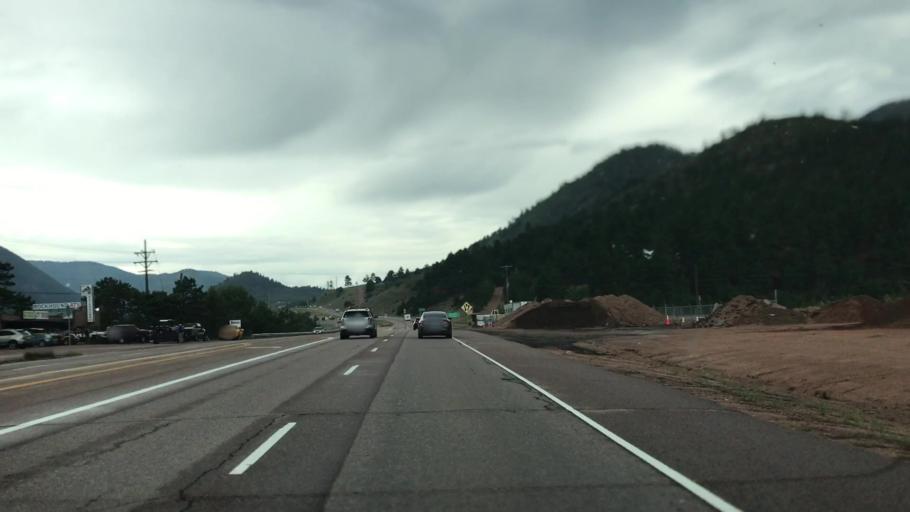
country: US
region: Colorado
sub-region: El Paso County
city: Cascade-Chipita Park
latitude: 38.9170
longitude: -104.9826
